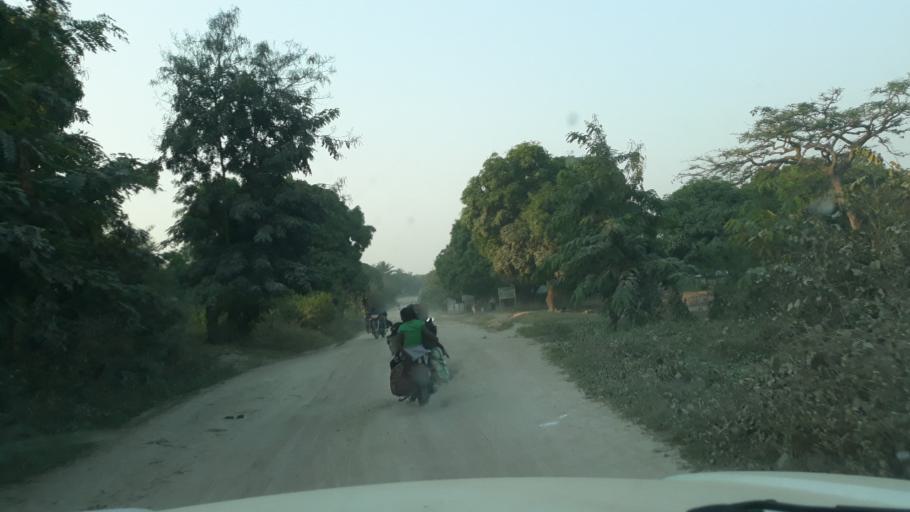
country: BI
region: Bururi
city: Rumonge
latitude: -4.1485
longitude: 29.0724
